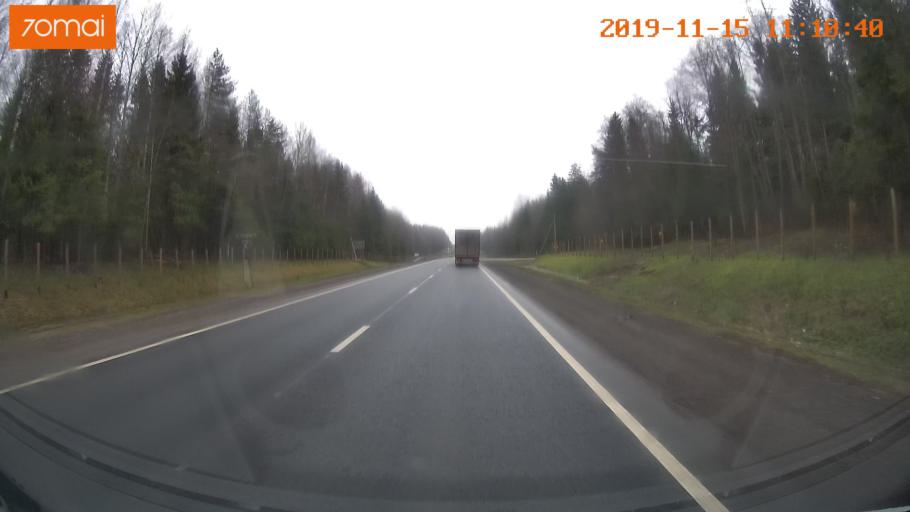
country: RU
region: Vologda
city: Chebsara
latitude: 59.1211
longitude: 39.1253
